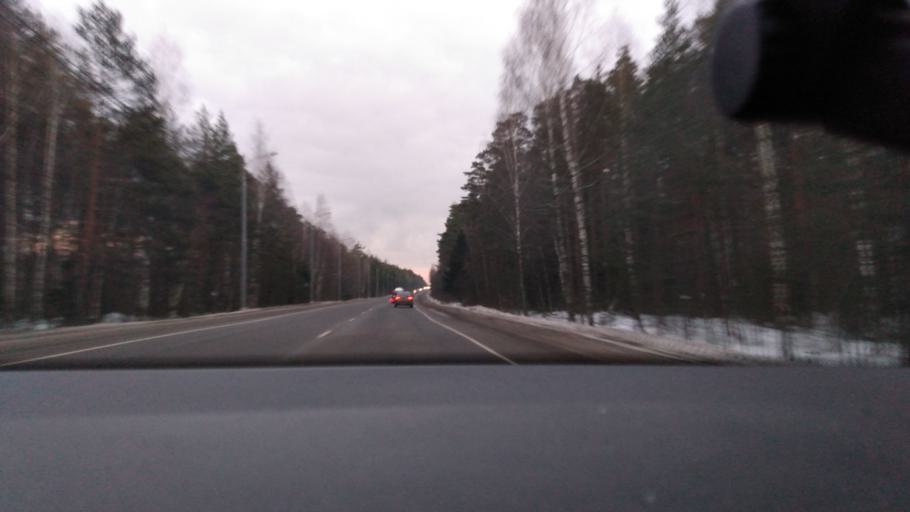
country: RU
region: Moskovskaya
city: Il'inskiy Pogost
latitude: 55.4742
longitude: 38.9543
